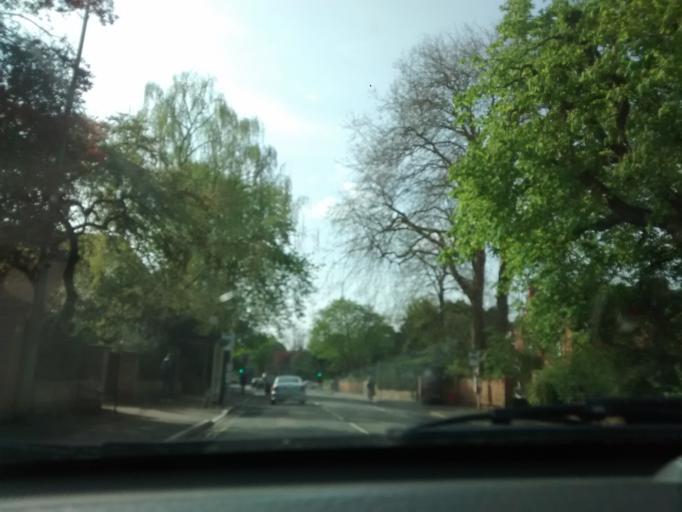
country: GB
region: England
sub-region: Oxfordshire
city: Oxford
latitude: 51.7682
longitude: -1.2656
